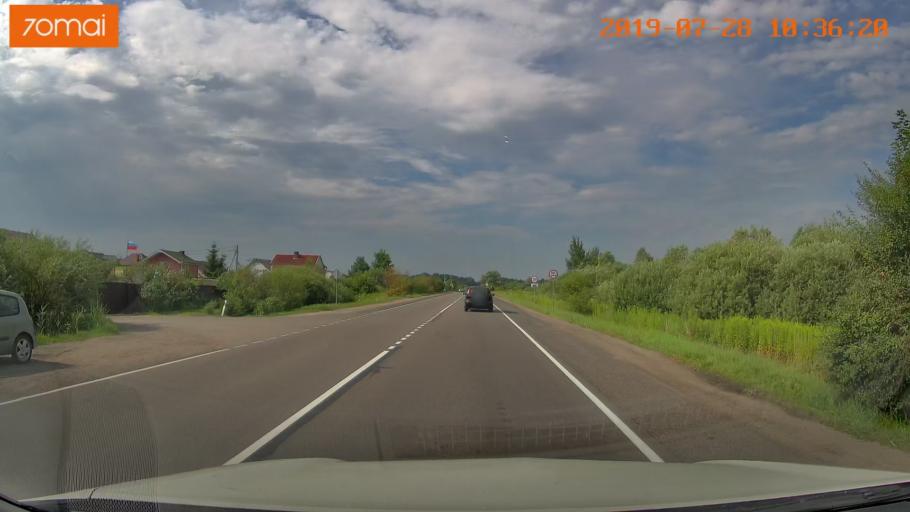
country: RU
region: Kaliningrad
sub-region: Gorod Kaliningrad
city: Kaliningrad
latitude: 54.7386
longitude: 20.4221
